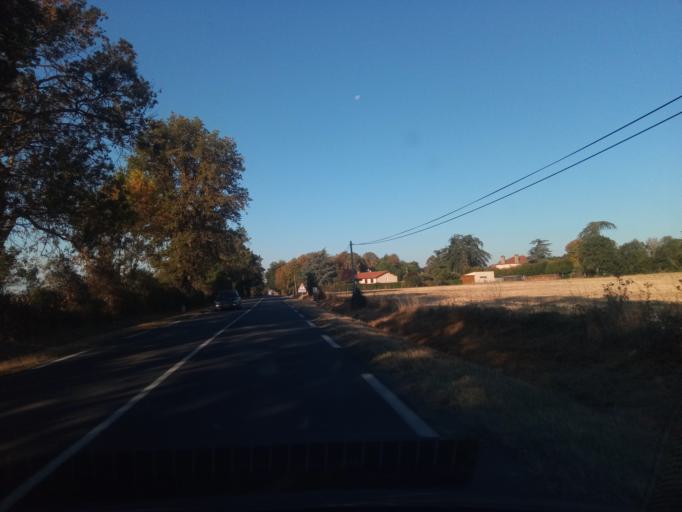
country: FR
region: Poitou-Charentes
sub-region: Departement de la Vienne
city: Lussac-les-Chateaux
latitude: 46.4075
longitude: 0.7975
